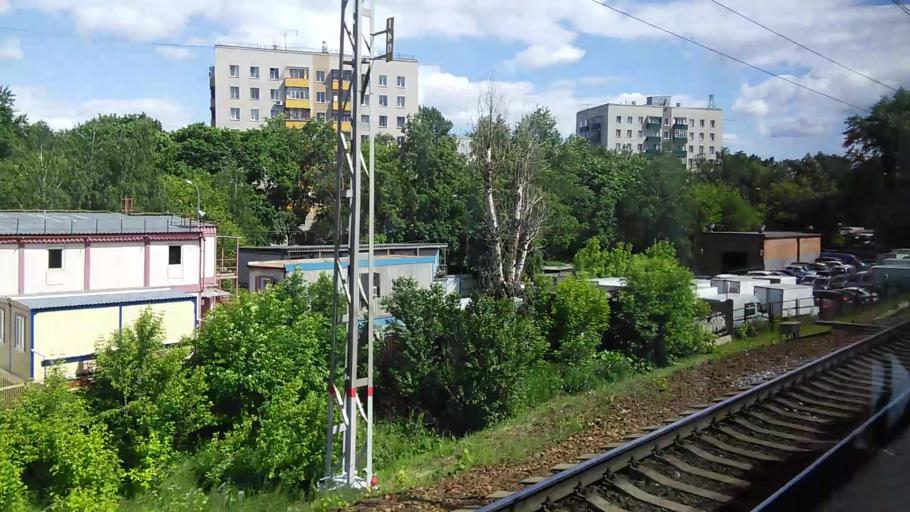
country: RU
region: Moscow
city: Novovladykino
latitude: 55.8423
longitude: 37.5771
